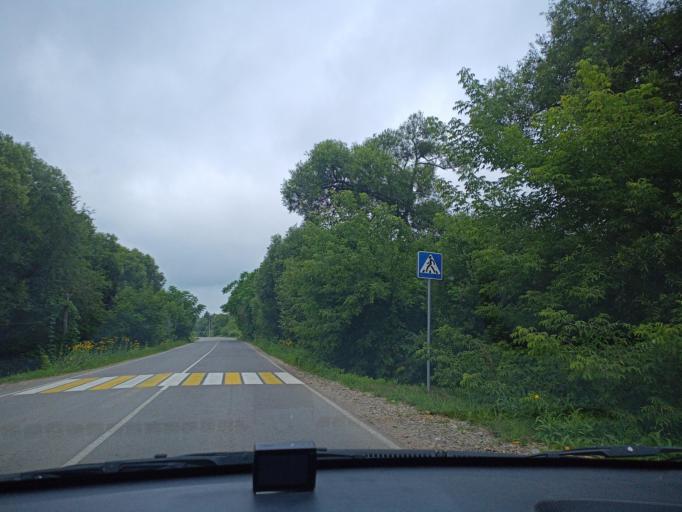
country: RU
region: Primorskiy
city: Novopokrovka
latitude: 45.8927
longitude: 134.8562
